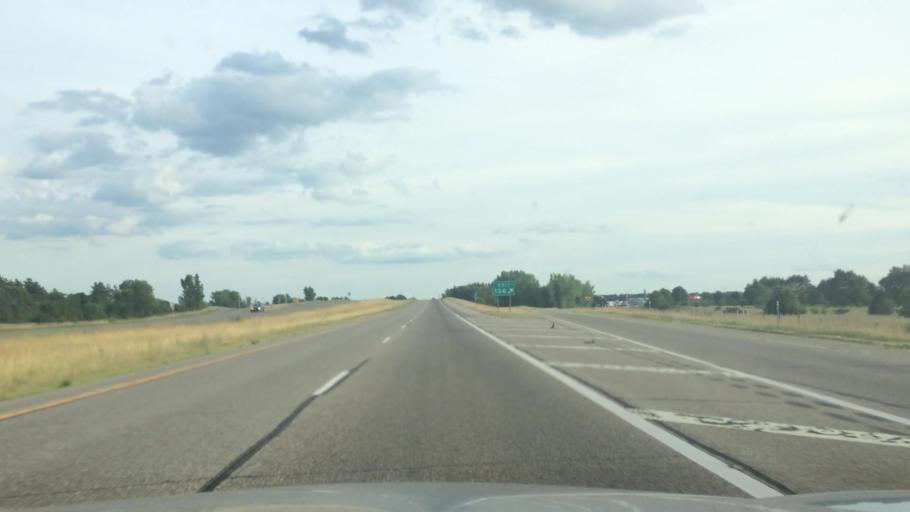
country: US
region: Wisconsin
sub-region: Portage County
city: Plover
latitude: 44.2184
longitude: -89.5248
